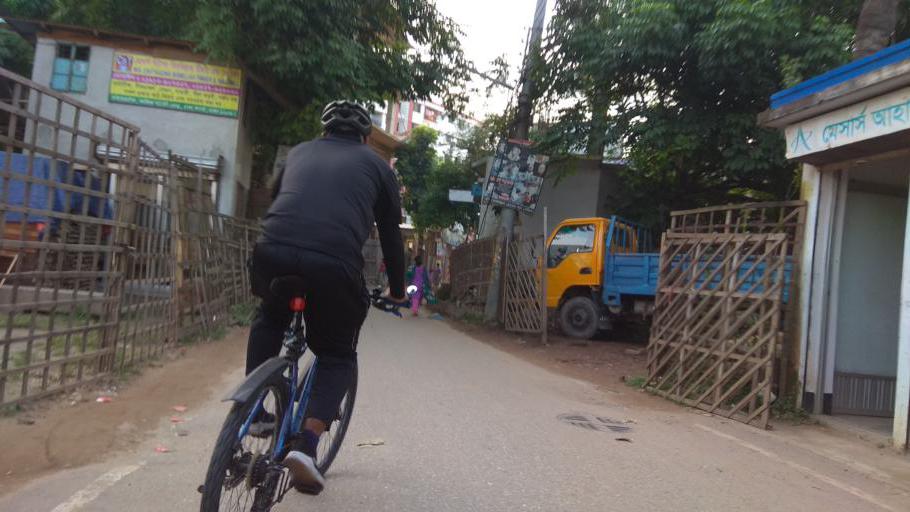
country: BD
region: Dhaka
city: Tungi
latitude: 23.8339
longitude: 90.3887
